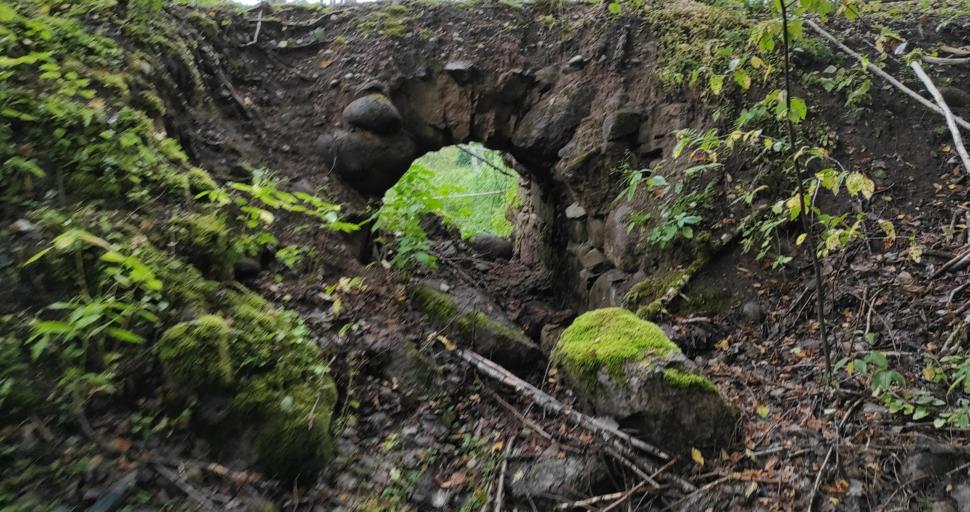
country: LV
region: Talsu Rajons
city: Talsi
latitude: 57.2044
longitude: 22.7240
